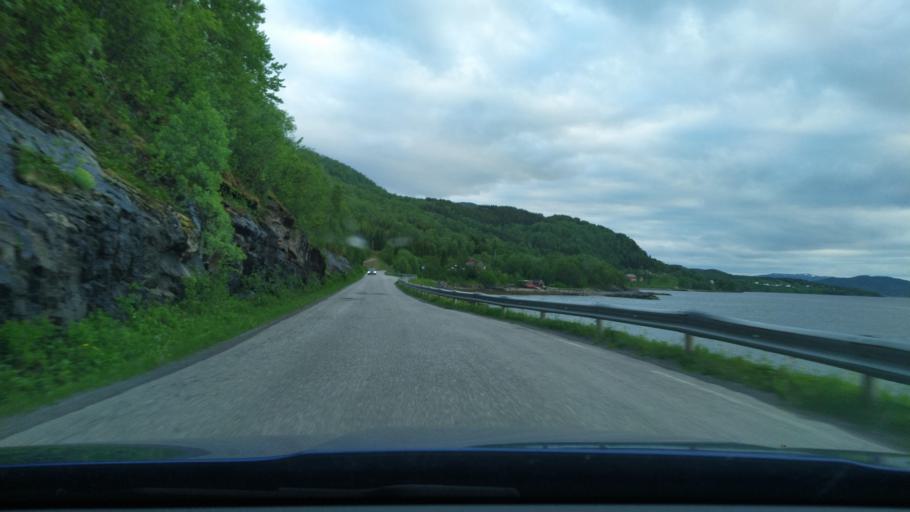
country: NO
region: Troms
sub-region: Lenvik
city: Finnsnes
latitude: 69.1392
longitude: 17.9085
